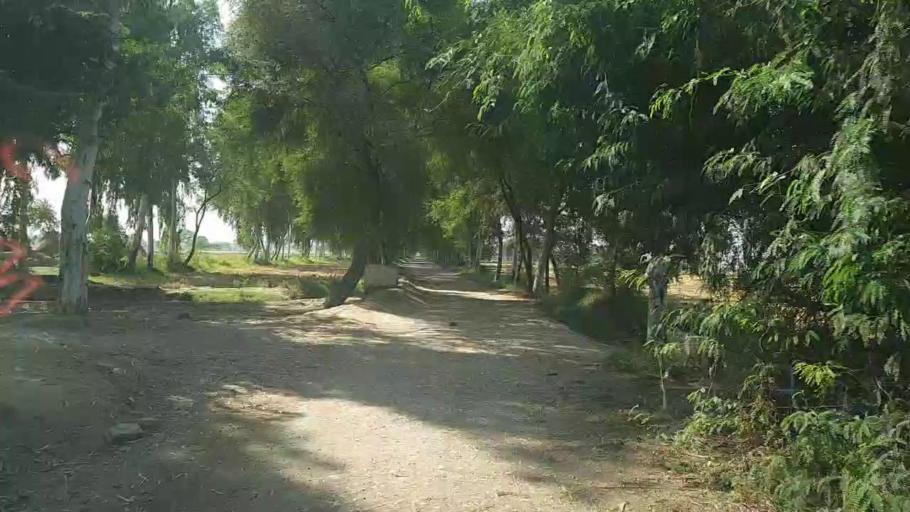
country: PK
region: Sindh
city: Thul
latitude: 28.2420
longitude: 68.7977
